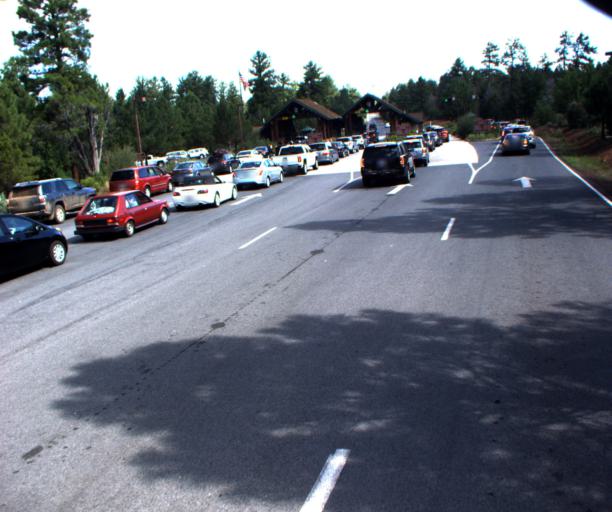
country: US
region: Arizona
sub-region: Coconino County
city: Grand Canyon Village
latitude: 35.9993
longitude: -112.1215
